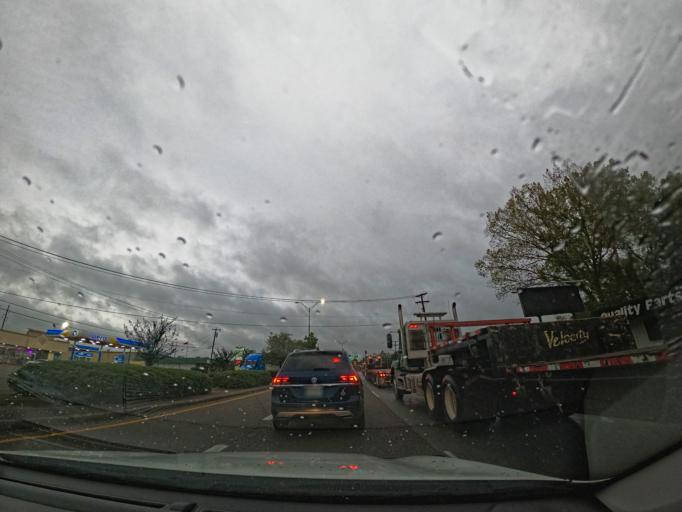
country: US
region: Texas
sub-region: Angelina County
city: Diboll
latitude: 31.1913
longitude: -94.7810
